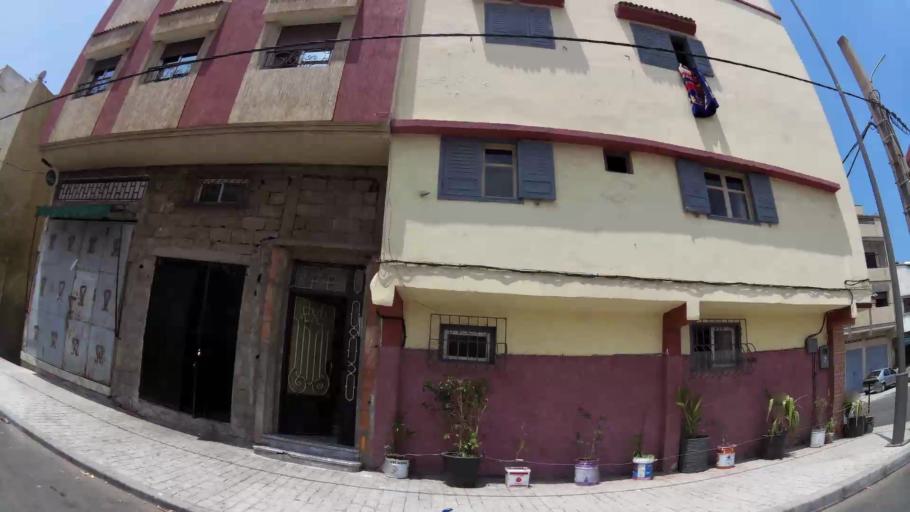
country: MA
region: Rabat-Sale-Zemmour-Zaer
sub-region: Rabat
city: Rabat
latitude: 33.9885
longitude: -6.8725
